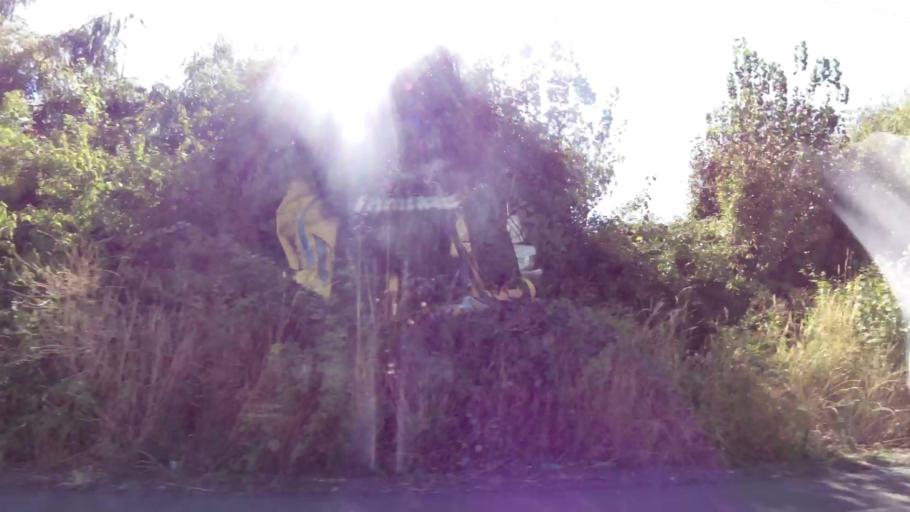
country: CL
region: Maule
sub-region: Provincia de Talca
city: Talca
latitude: -35.4164
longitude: -71.5959
